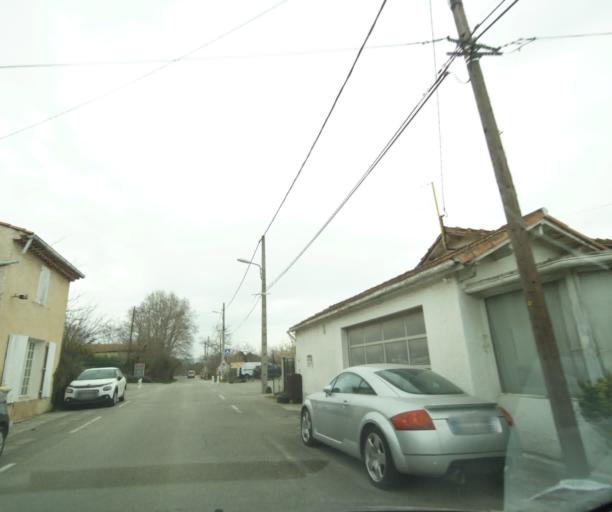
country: FR
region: Provence-Alpes-Cote d'Azur
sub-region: Departement des Bouches-du-Rhone
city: Aix-en-Provence
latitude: 43.5770
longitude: 5.4306
